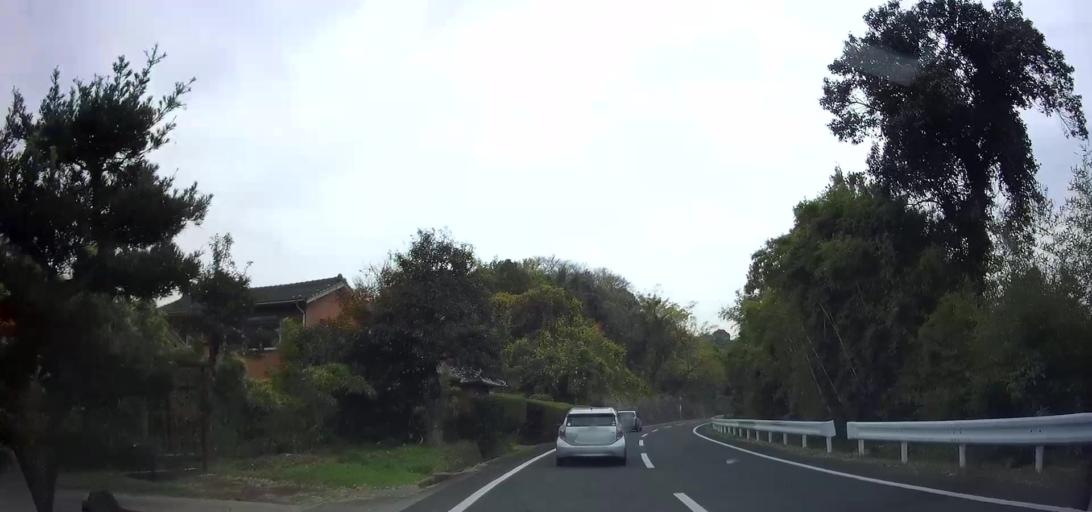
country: JP
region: Nagasaki
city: Shimabara
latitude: 32.6663
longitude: 130.2989
